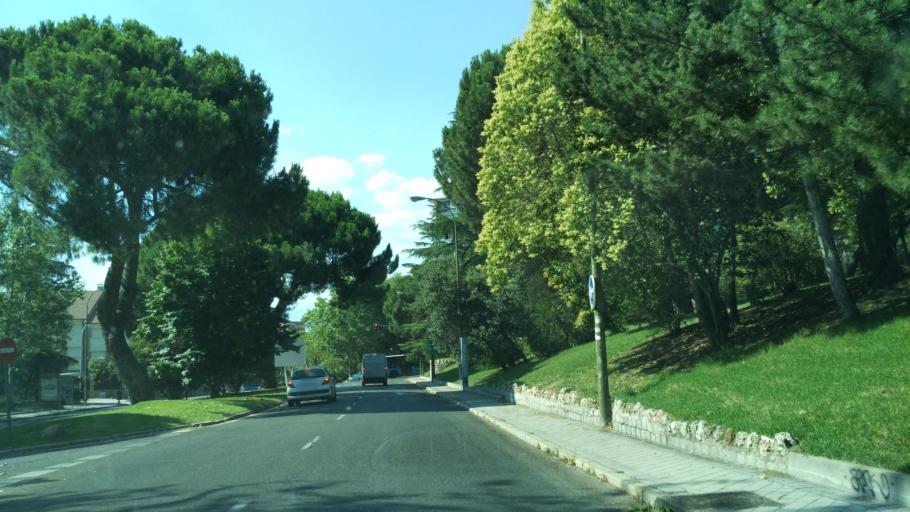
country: ES
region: Madrid
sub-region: Provincia de Madrid
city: Tetuan de las Victorias
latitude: 40.4613
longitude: -3.7189
